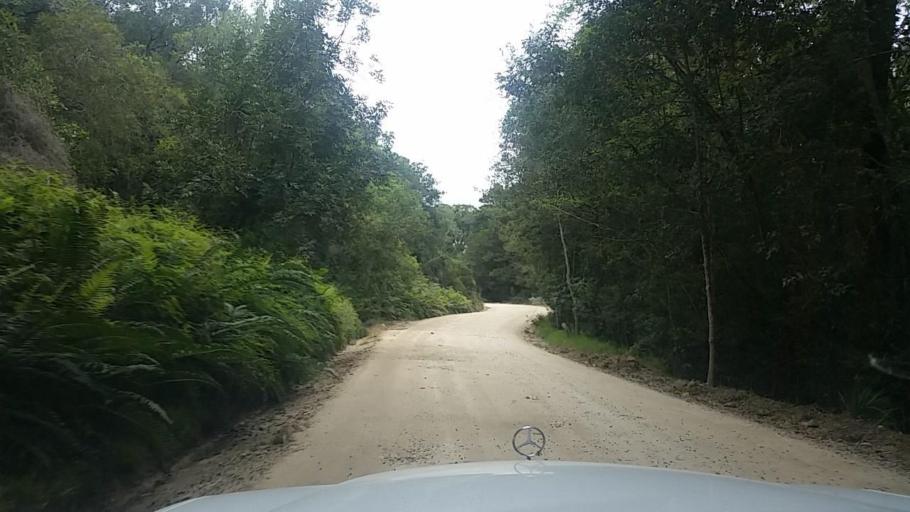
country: ZA
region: Western Cape
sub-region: Eden District Municipality
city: Knysna
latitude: -33.9507
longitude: 23.1482
